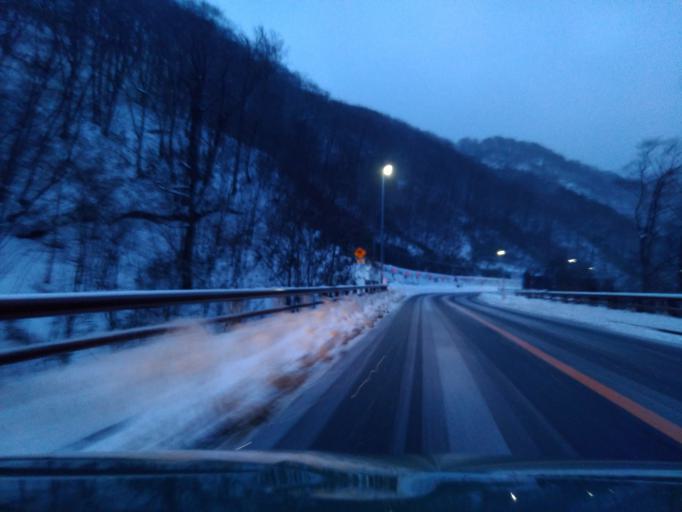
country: JP
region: Iwate
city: Shizukuishi
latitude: 39.7192
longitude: 140.8213
